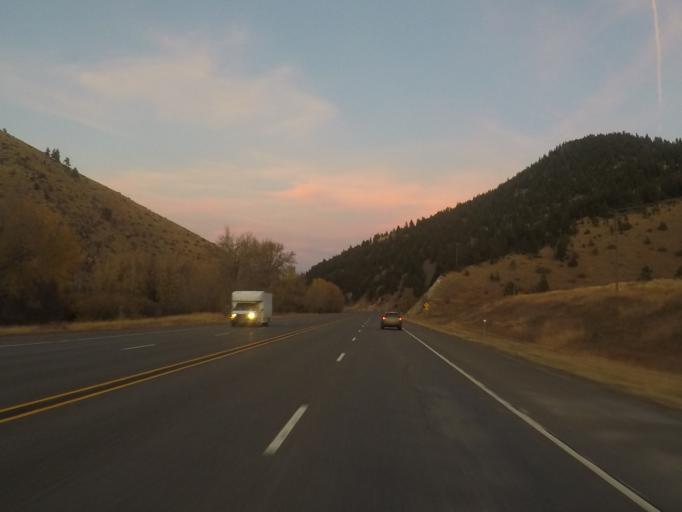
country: US
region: Montana
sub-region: Lewis and Clark County
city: Helena West Side
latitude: 46.5885
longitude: -112.1245
